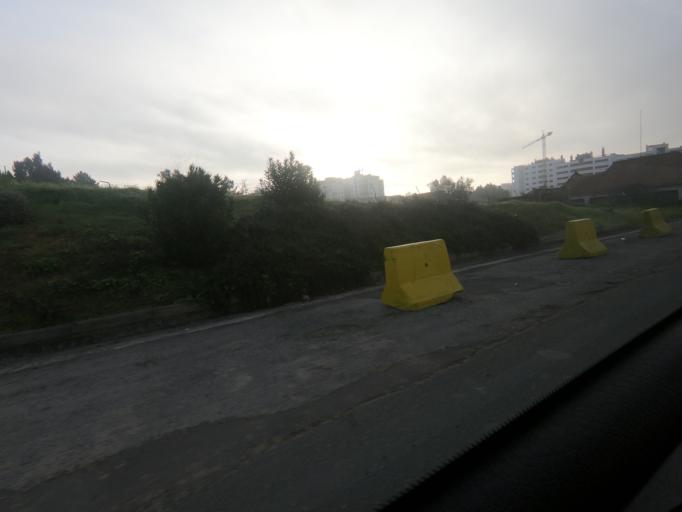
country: PT
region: Setubal
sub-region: Setubal
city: Setubal
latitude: 38.5338
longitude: -8.8753
